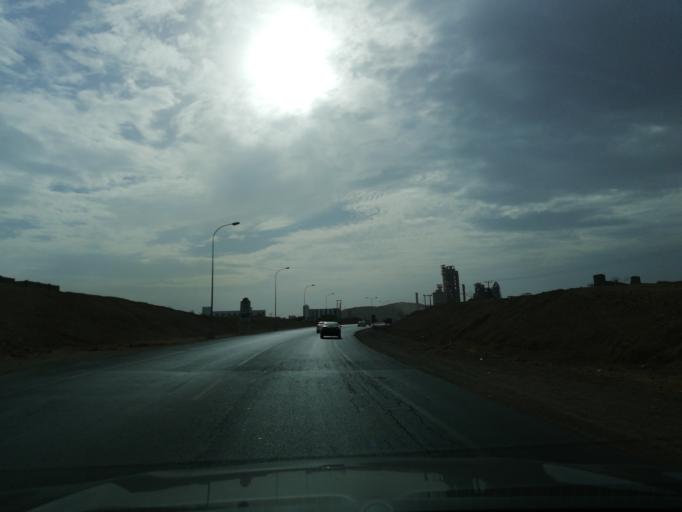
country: OM
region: Muhafazat Masqat
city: Bawshar
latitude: 23.4785
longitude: 58.2901
